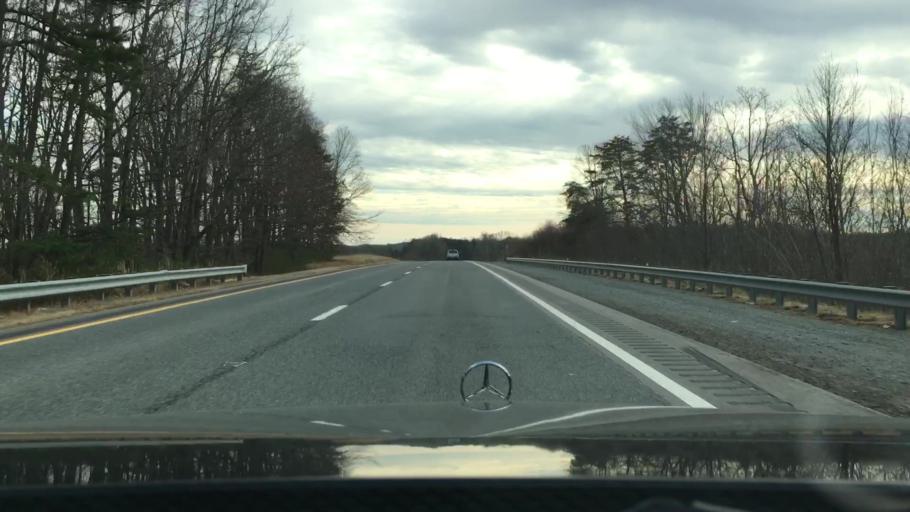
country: US
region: Virginia
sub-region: Pittsylvania County
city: Gretna
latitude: 36.9365
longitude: -79.3768
